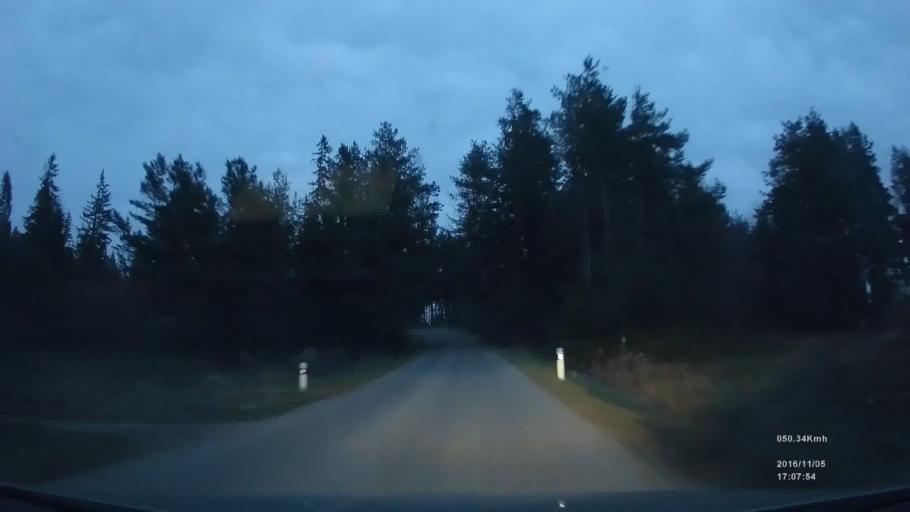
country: SK
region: Presovsky
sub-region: Okres Presov
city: Levoca
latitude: 49.0461
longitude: 20.5091
